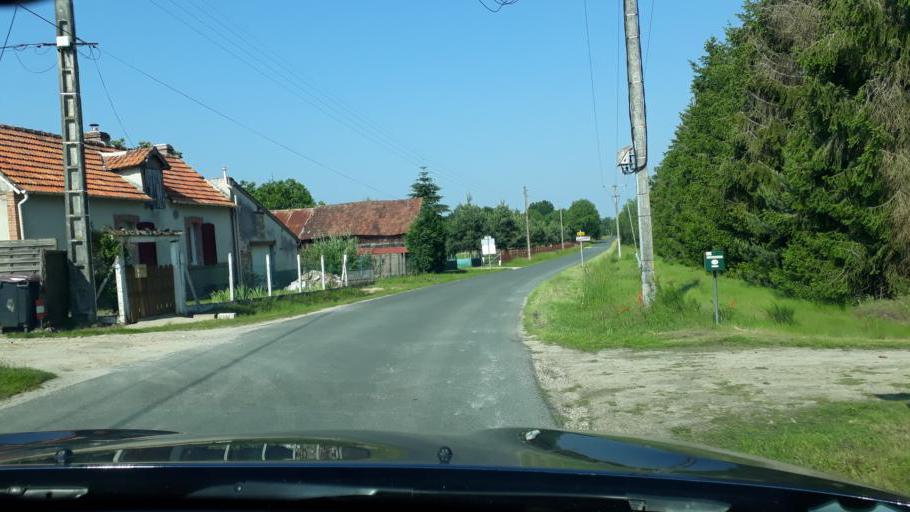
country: FR
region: Centre
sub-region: Departement du Loiret
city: Ligny-le-Ribault
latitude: 47.6216
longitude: 1.7465
